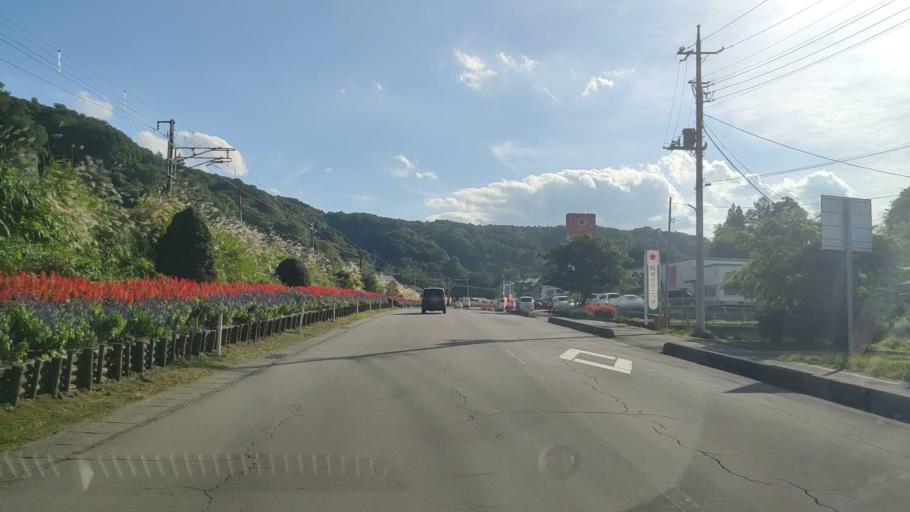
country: JP
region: Nagano
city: Komoro
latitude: 36.5226
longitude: 138.5421
